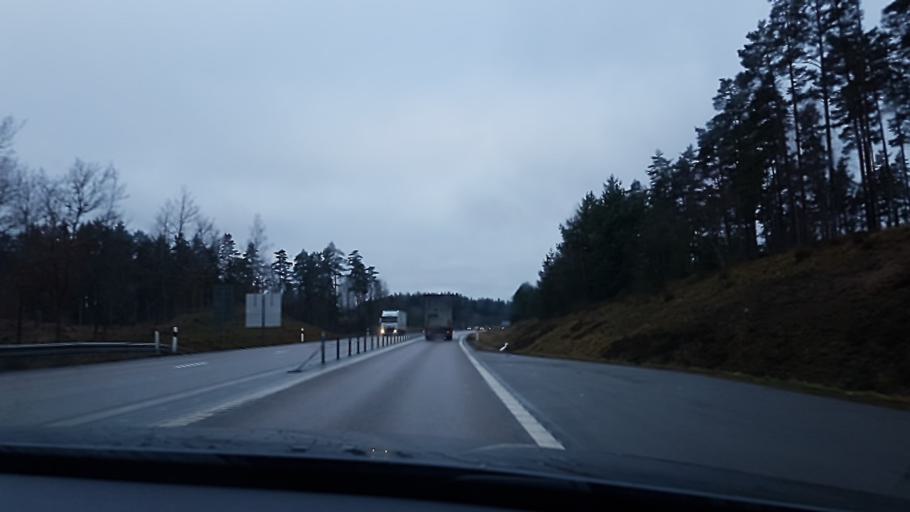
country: SE
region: Kronoberg
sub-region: Ljungby Kommun
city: Lagan
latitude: 56.9424
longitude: 13.9977
